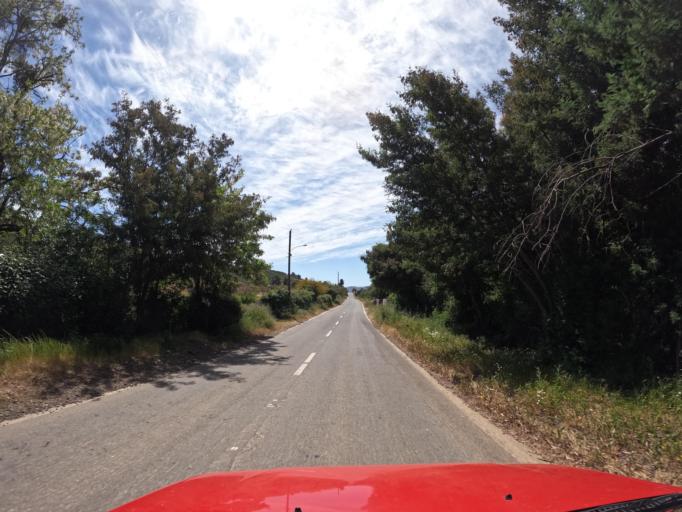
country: CL
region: Maule
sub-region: Provincia de Talca
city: Talca
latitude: -35.0480
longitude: -71.7505
